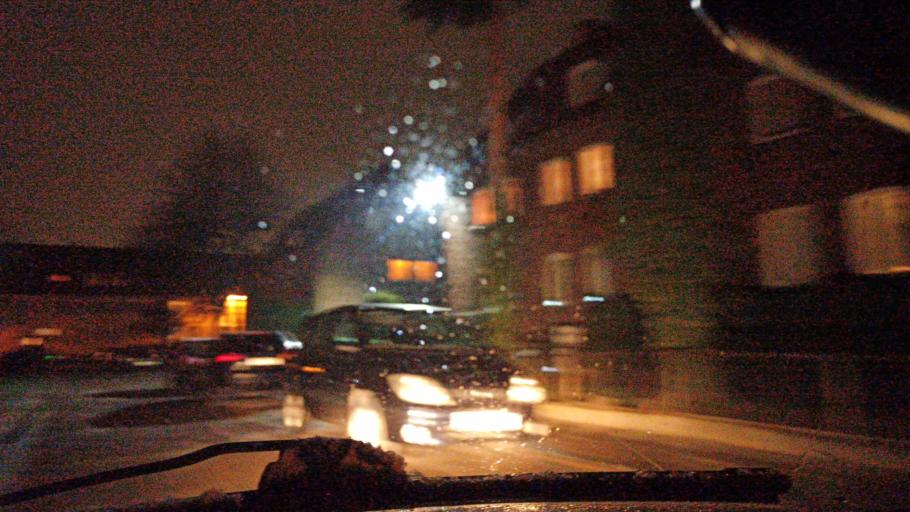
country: PL
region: Warmian-Masurian Voivodeship
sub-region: Powiat elblaski
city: Gronowo Gorne
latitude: 54.1538
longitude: 19.4451
